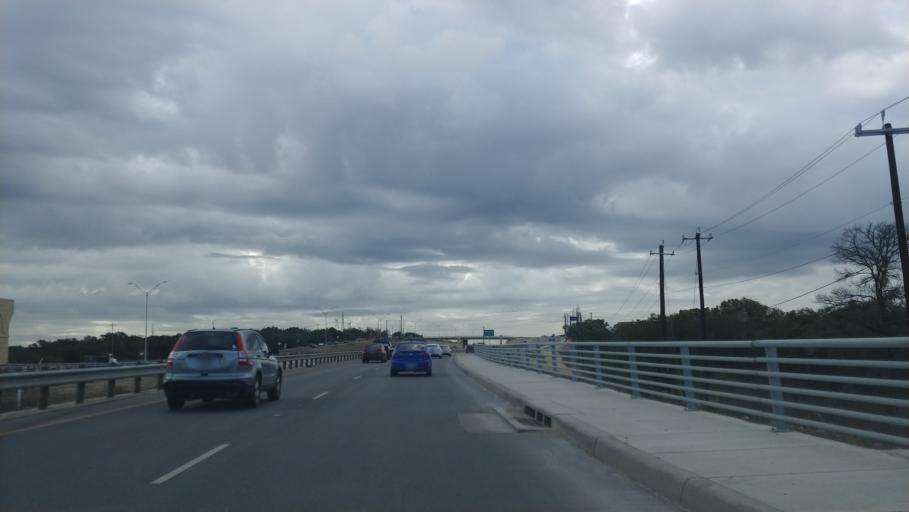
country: US
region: Texas
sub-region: Bexar County
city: Lackland Air Force Base
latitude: 29.4221
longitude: -98.7104
